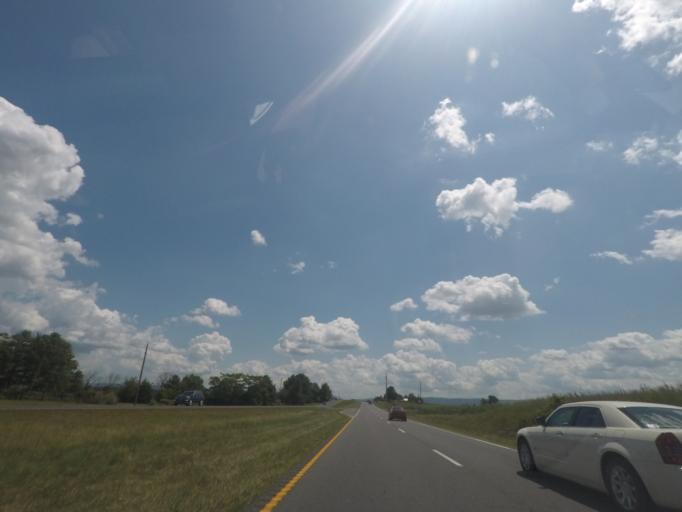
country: US
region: Virginia
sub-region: Warren County
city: Shenandoah Farms
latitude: 39.0913
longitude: -78.0976
